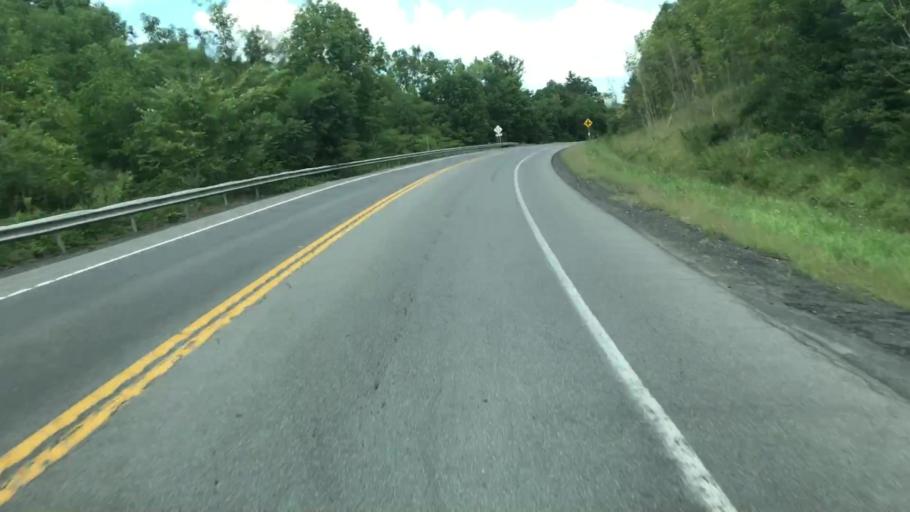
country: US
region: New York
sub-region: Onondaga County
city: Marcellus
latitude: 42.9733
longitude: -76.3359
